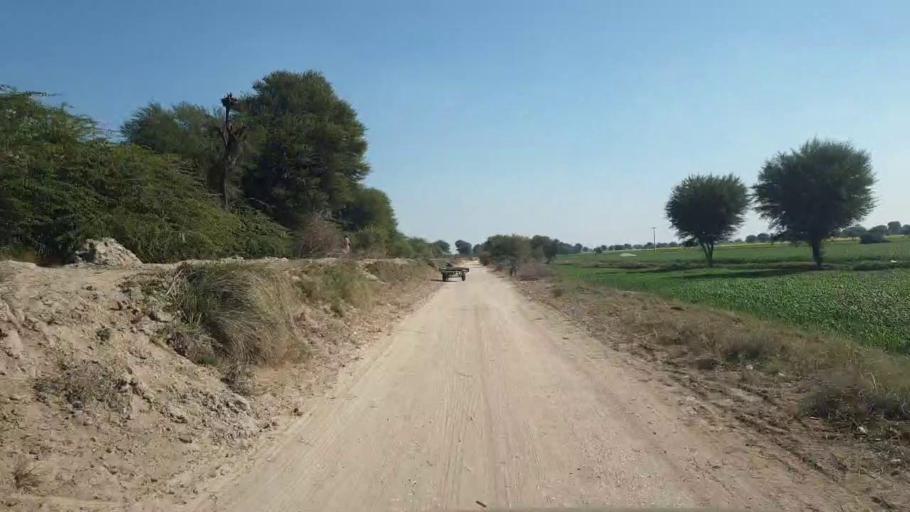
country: PK
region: Sindh
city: Shahpur Chakar
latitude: 26.1442
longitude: 68.6499
